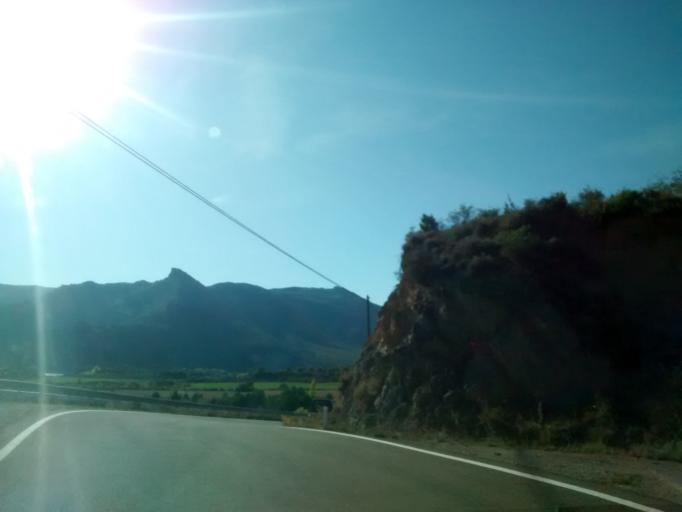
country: ES
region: Aragon
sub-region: Provincia de Zaragoza
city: Santa Eulalia de Gallego
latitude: 42.3893
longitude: -0.7197
